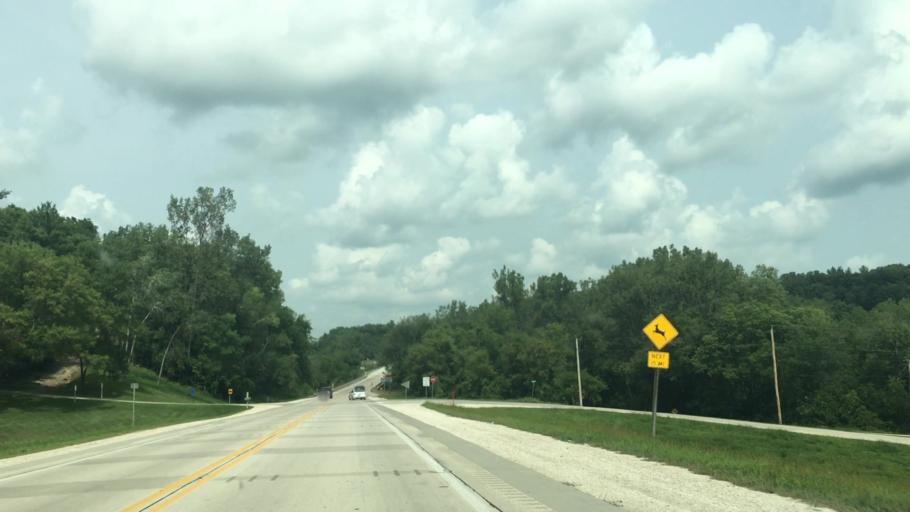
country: US
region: Iowa
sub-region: Winneshiek County
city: Decorah
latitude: 43.2966
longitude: -91.8097
